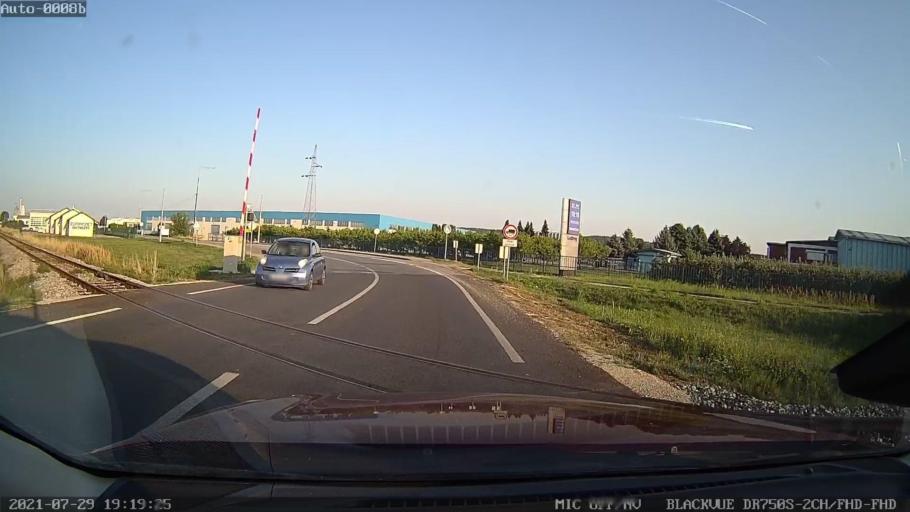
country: HR
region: Varazdinska
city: Ludbreg
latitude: 46.2578
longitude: 16.5984
